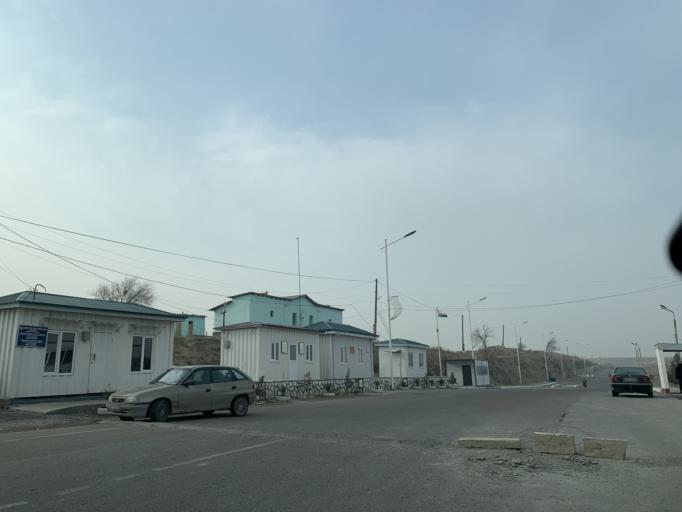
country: UZ
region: Toshkent
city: Bekobod
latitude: 40.2119
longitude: 69.2063
